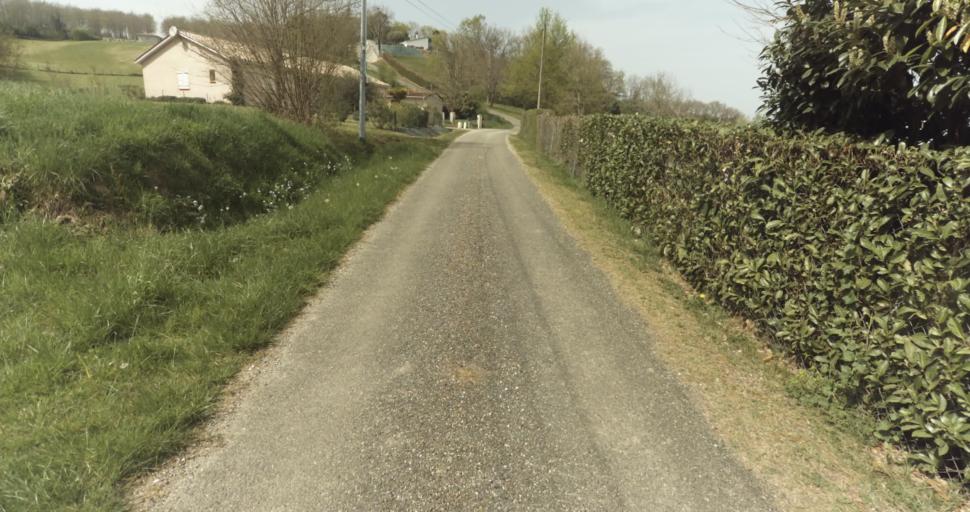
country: FR
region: Midi-Pyrenees
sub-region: Departement du Tarn-et-Garonne
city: Moissac
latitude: 44.1198
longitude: 1.1021
